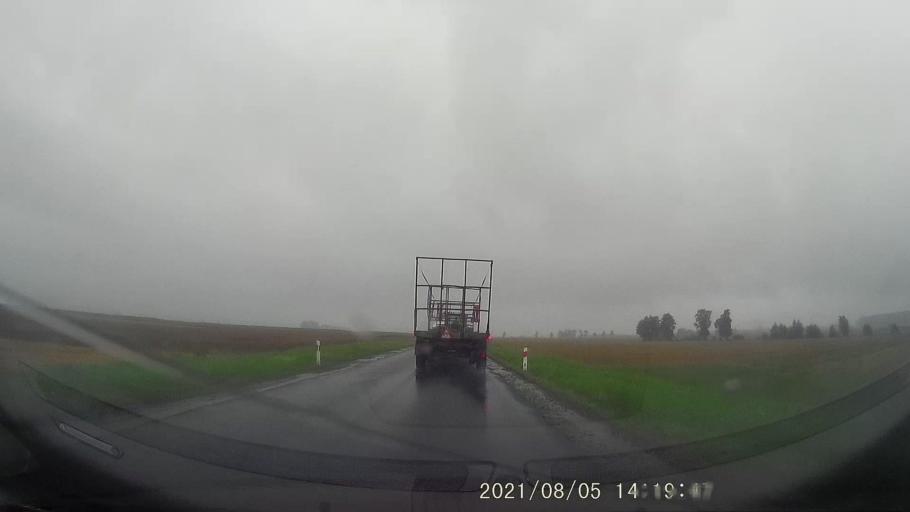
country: PL
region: Opole Voivodeship
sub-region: Powiat prudnicki
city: Biala
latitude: 50.4676
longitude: 17.6847
